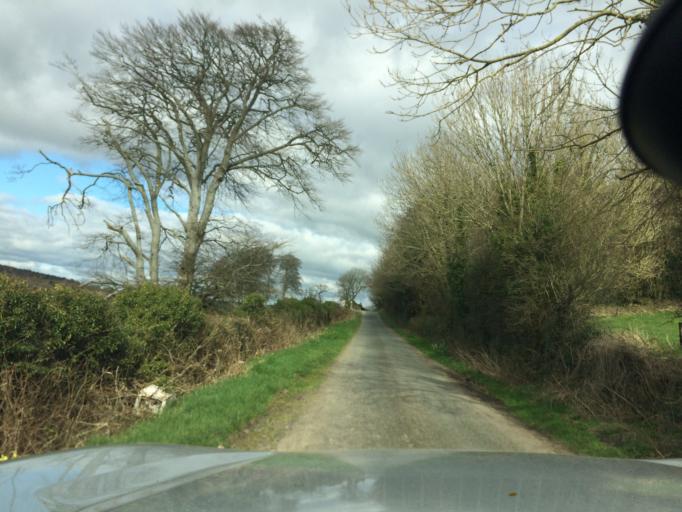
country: IE
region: Munster
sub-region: Waterford
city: Portlaw
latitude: 52.2824
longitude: -7.3481
